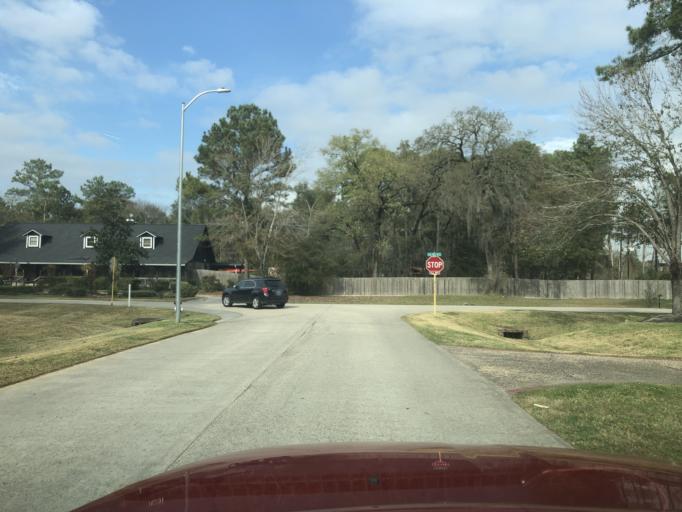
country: US
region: Texas
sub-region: Harris County
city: Spring
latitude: 30.0243
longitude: -95.4666
